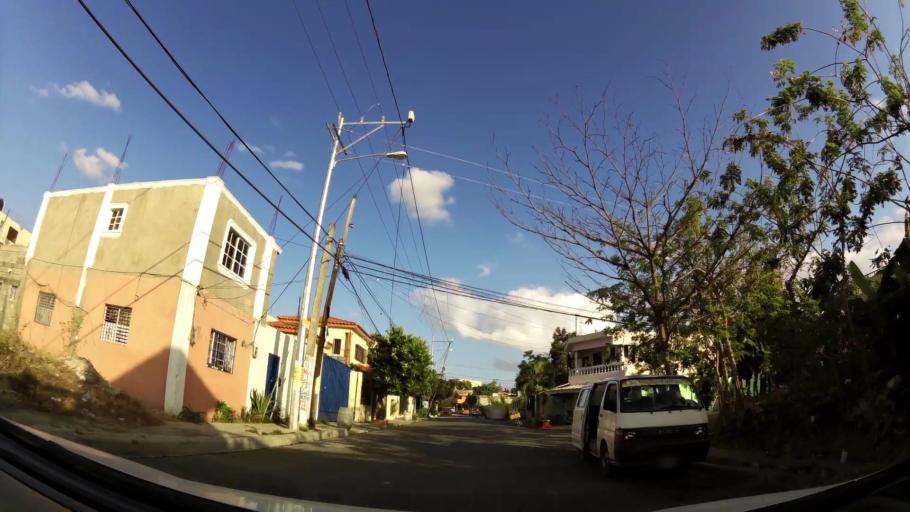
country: DO
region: Nacional
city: Ensanche Luperon
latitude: 18.5457
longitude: -69.9035
